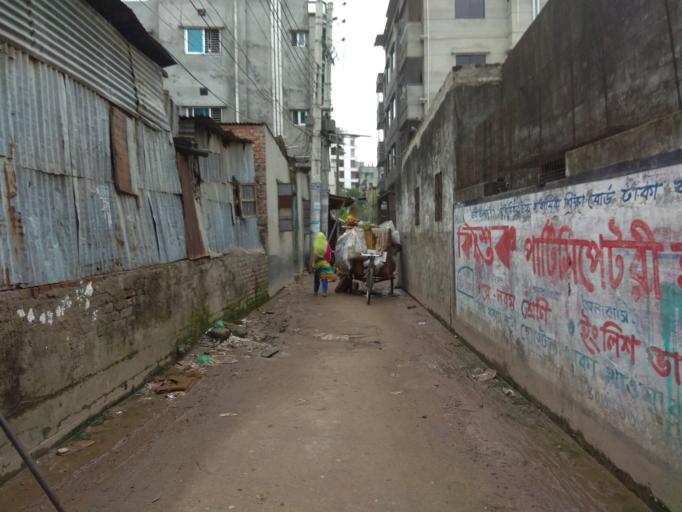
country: BD
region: Dhaka
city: Azimpur
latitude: 23.7958
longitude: 90.3691
